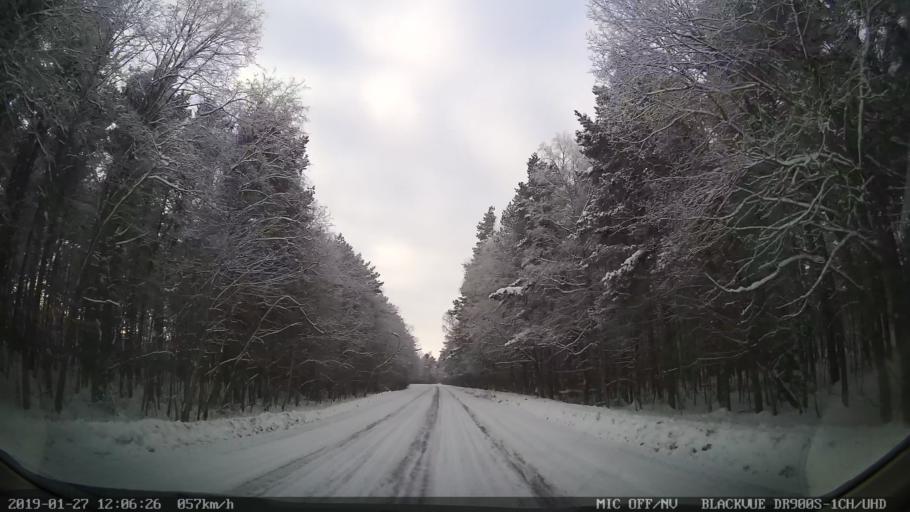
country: EE
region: Harju
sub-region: Raasiku vald
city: Raasiku
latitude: 59.4719
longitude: 25.2444
